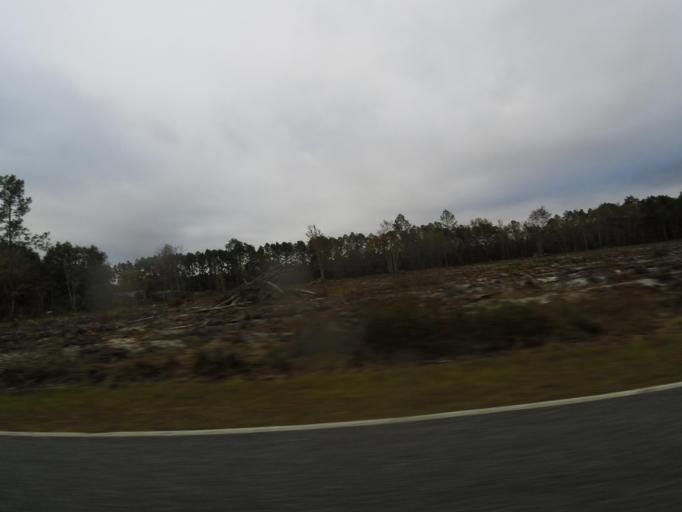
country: US
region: Georgia
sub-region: Charlton County
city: Folkston
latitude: 30.8791
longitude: -82.0517
